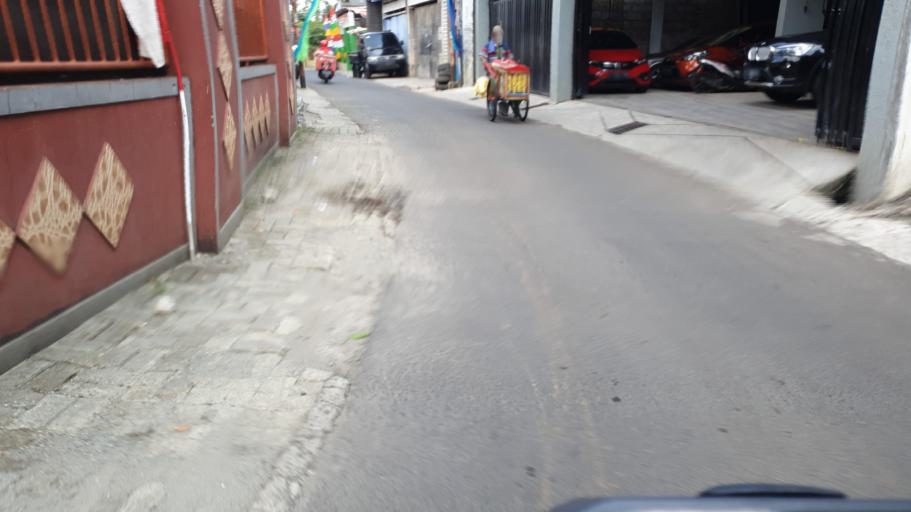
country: ID
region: West Java
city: Depok
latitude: -6.3696
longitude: 106.8514
